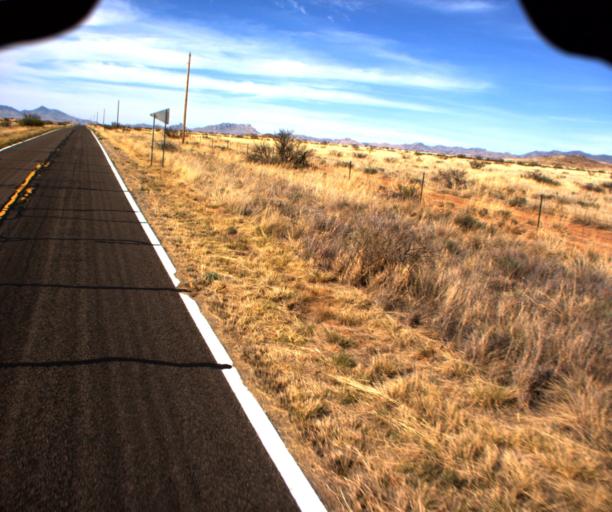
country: US
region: Arizona
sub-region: Cochise County
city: Willcox
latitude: 31.9220
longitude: -109.4914
